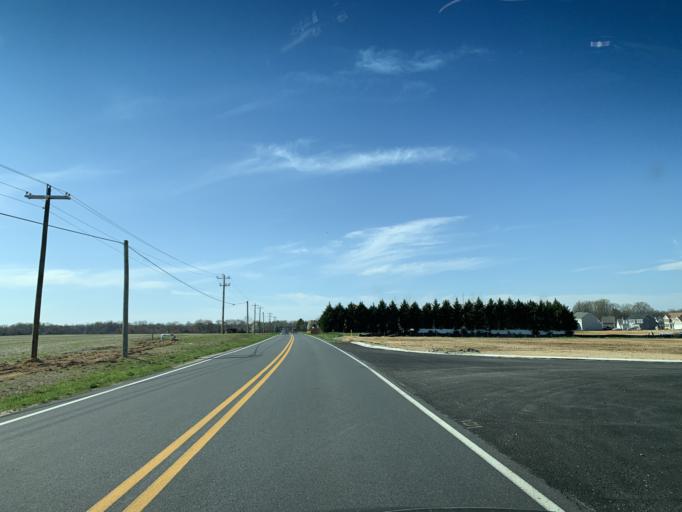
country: US
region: Delaware
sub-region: Kent County
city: Riverview
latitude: 38.9803
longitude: -75.5026
